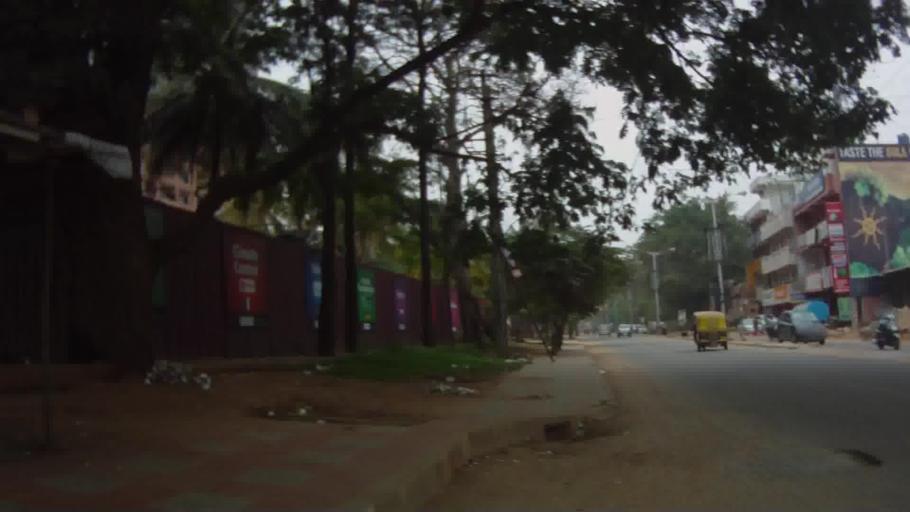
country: IN
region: Karnataka
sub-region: Bangalore Rural
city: Hoskote
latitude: 12.9563
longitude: 77.7316
